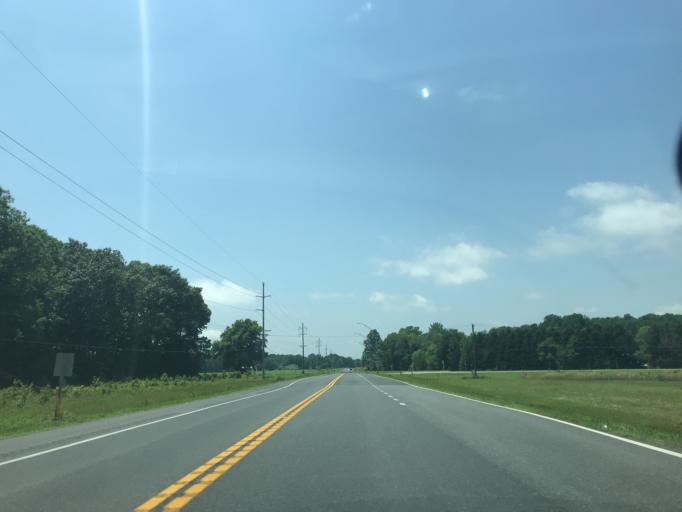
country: US
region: Maryland
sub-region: Dorchester County
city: Hurlock
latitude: 38.5914
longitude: -75.9318
